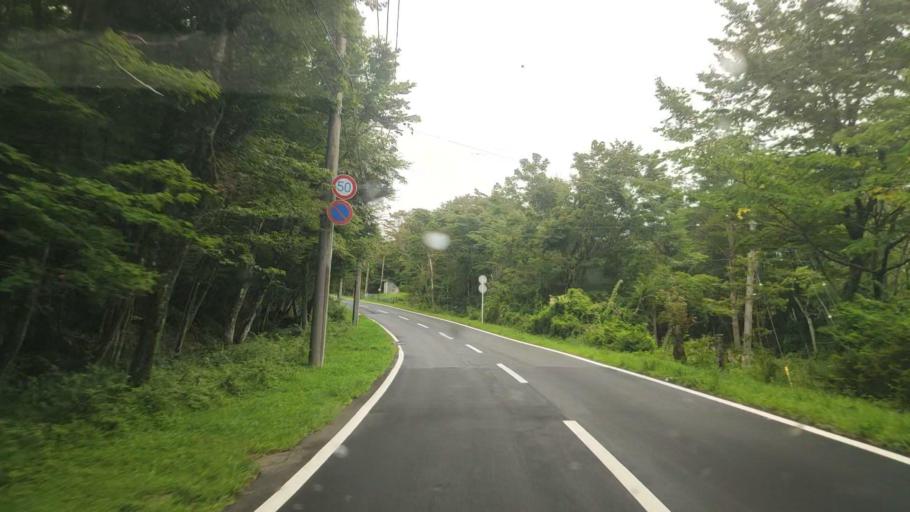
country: JP
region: Shizuoka
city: Gotemba
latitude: 35.2687
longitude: 138.8027
